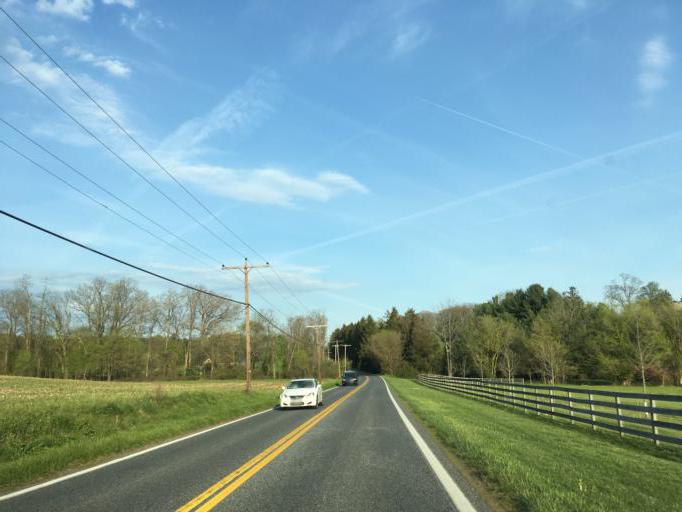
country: US
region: Maryland
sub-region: Baltimore County
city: Reisterstown
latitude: 39.4811
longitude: -76.7819
